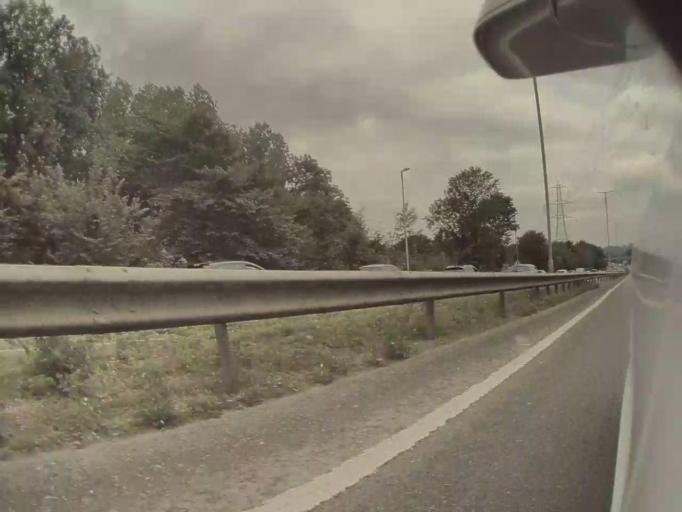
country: GB
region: Wales
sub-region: Anglesey
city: Menai Bridge
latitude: 53.2089
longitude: -4.1776
